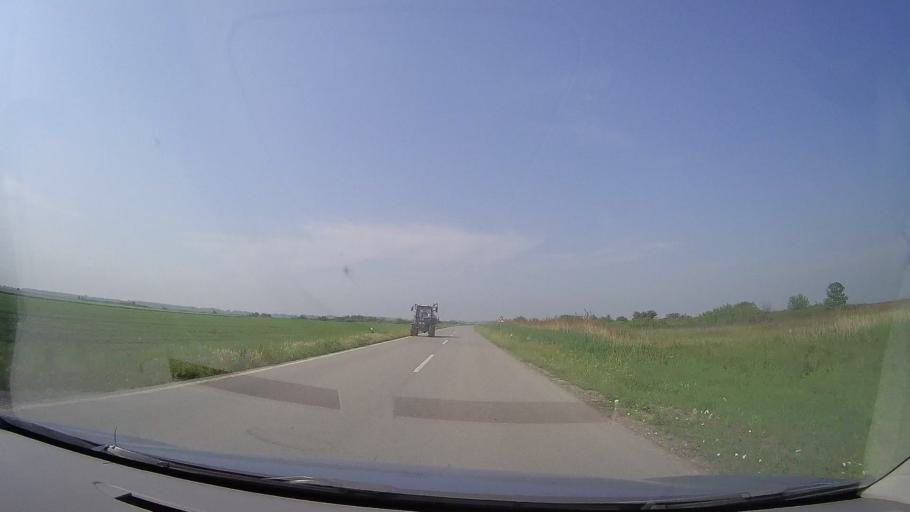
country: RS
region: Autonomna Pokrajina Vojvodina
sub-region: Srednjebanatski Okrug
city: Secanj
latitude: 45.3902
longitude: 20.8022
